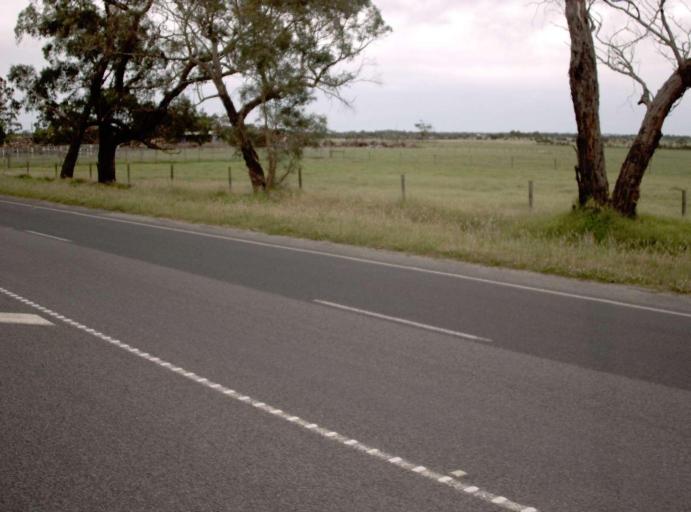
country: AU
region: Victoria
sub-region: Cardinia
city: Koo-Wee-Rup
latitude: -38.3180
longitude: 145.5844
